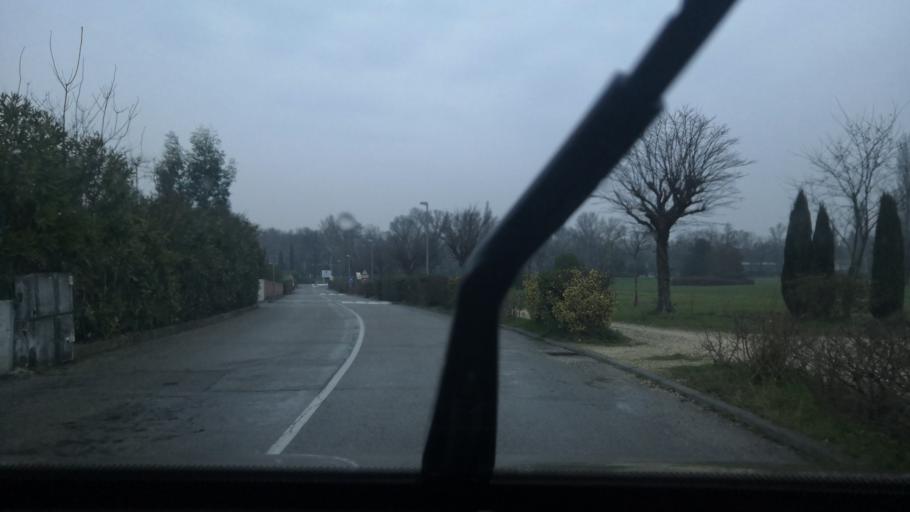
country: FR
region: Rhone-Alpes
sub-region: Departement de la Drome
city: Montboucher-sur-Jabron
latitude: 44.5429
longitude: 4.8024
